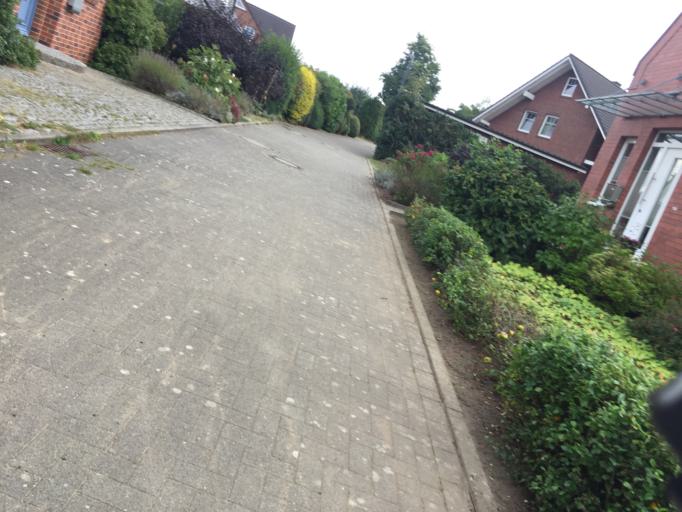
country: DE
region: Schleswig-Holstein
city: Itzehoe
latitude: 53.9340
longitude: 9.5310
